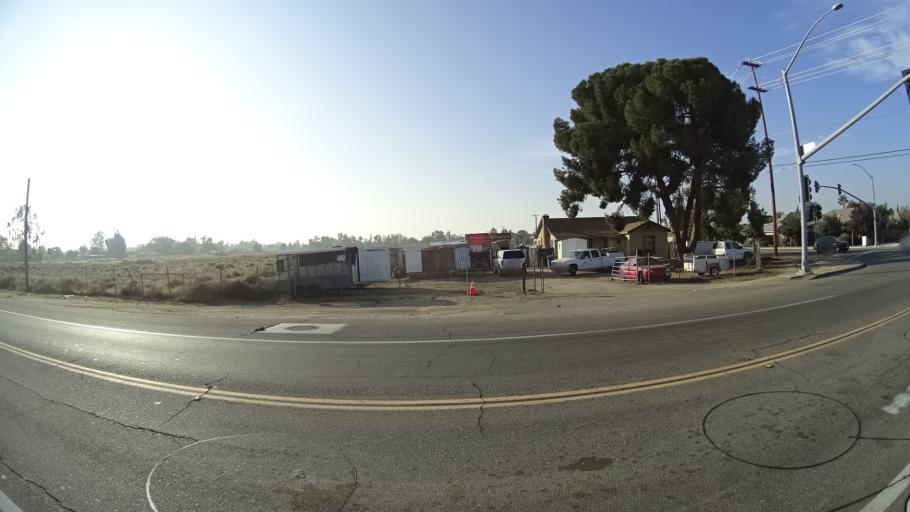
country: US
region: California
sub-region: Kern County
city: Rosedale
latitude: 35.3836
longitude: -119.1629
